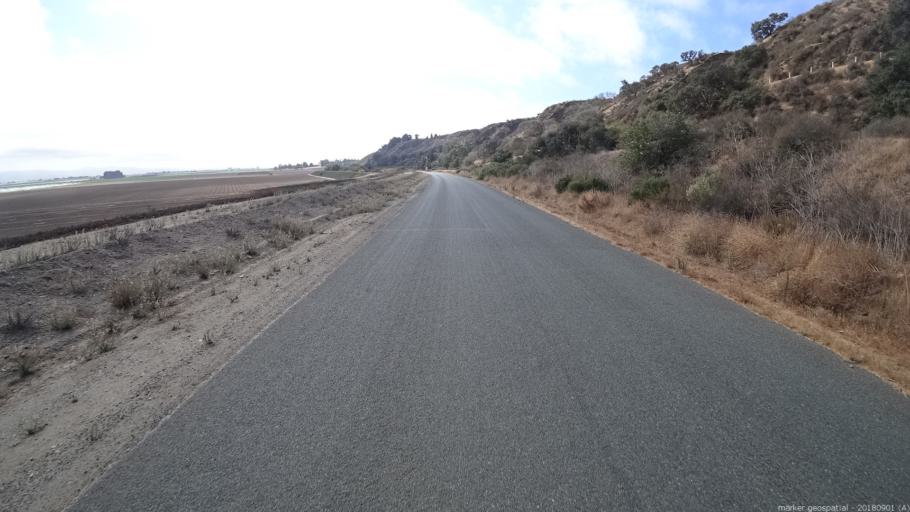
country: US
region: California
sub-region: Monterey County
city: Soledad
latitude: 36.4018
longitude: -121.3786
